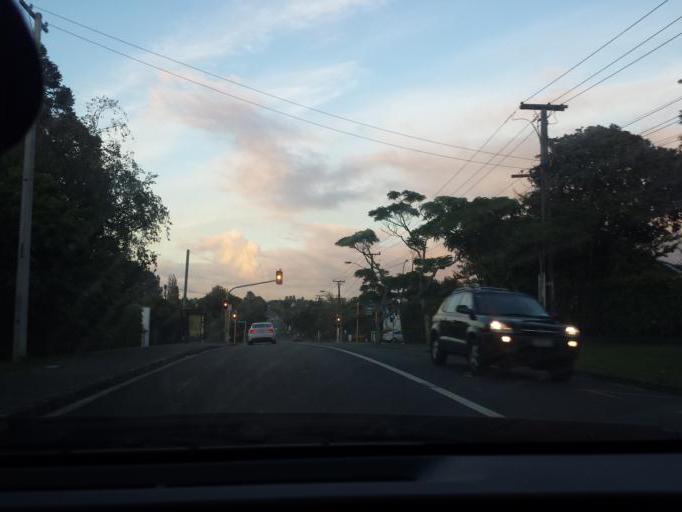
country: NZ
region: Auckland
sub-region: Auckland
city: Tamaki
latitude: -36.8623
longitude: 174.8570
